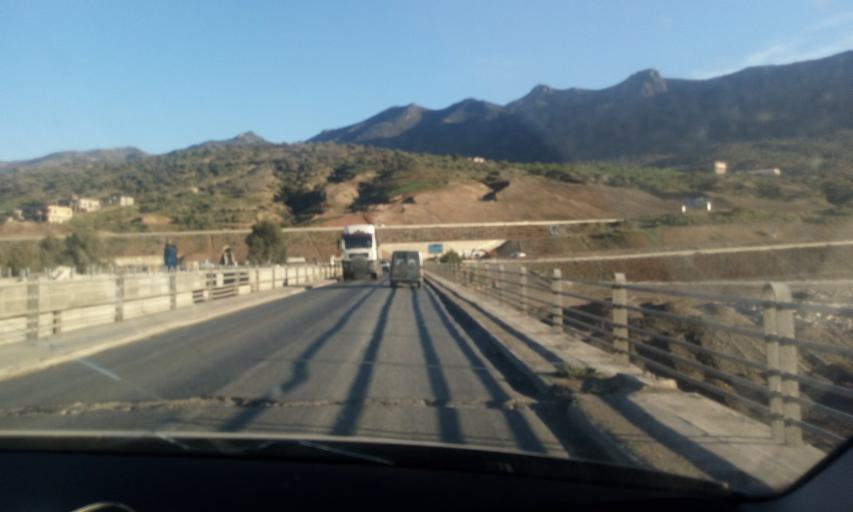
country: DZ
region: Bejaia
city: Akbou
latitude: 36.4811
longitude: 4.5923
